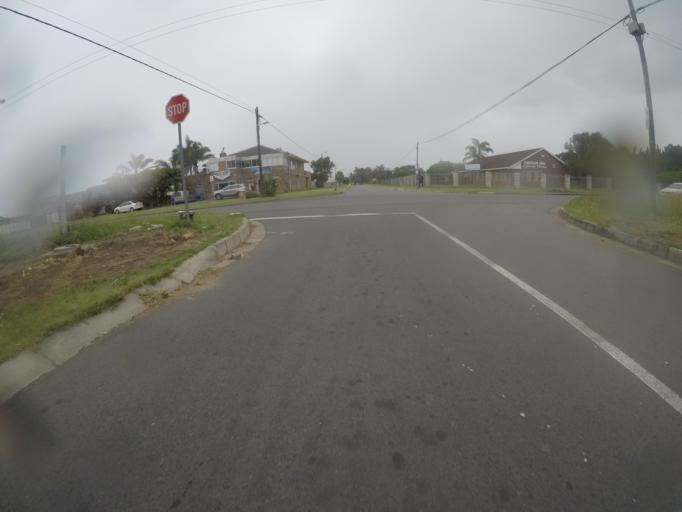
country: ZA
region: Eastern Cape
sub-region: Buffalo City Metropolitan Municipality
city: East London
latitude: -32.9503
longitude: 27.9974
